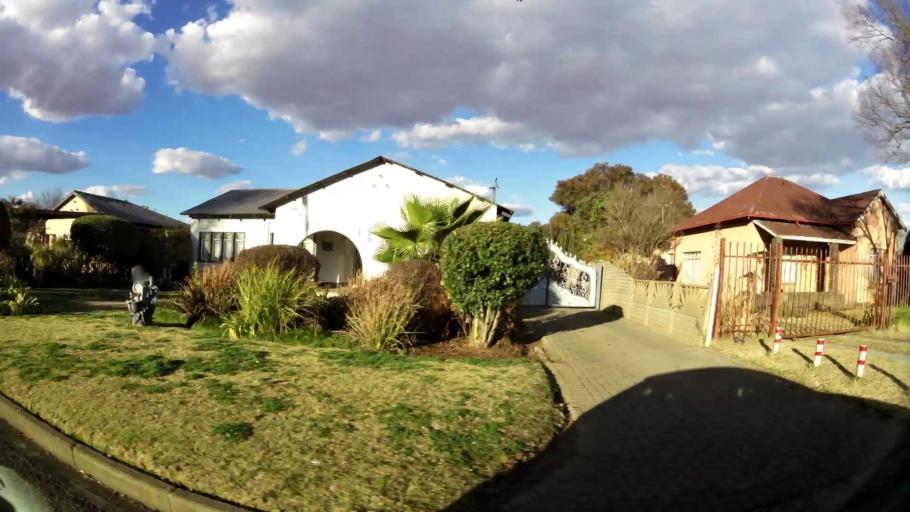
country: ZA
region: North-West
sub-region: Dr Kenneth Kaunda District Municipality
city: Potchefstroom
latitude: -26.7364
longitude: 27.0837
